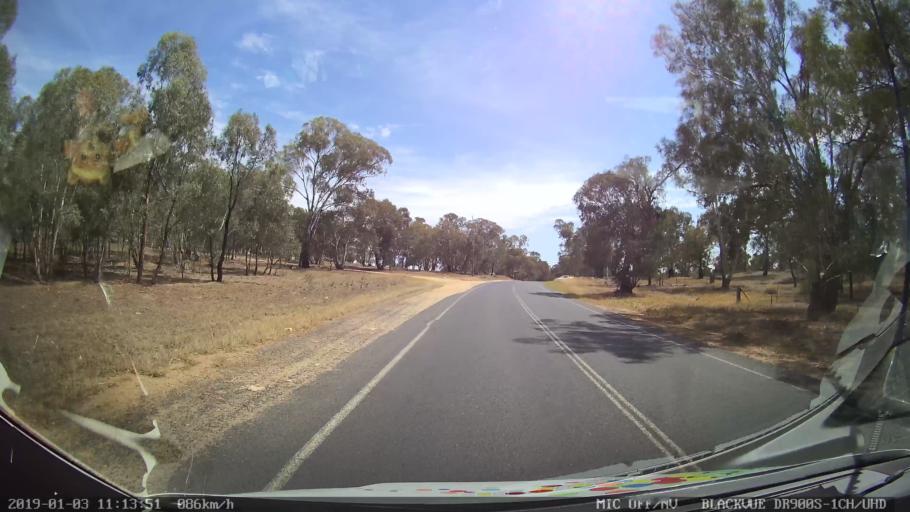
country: AU
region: New South Wales
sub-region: Young
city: Young
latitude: -34.1834
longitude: 148.2598
